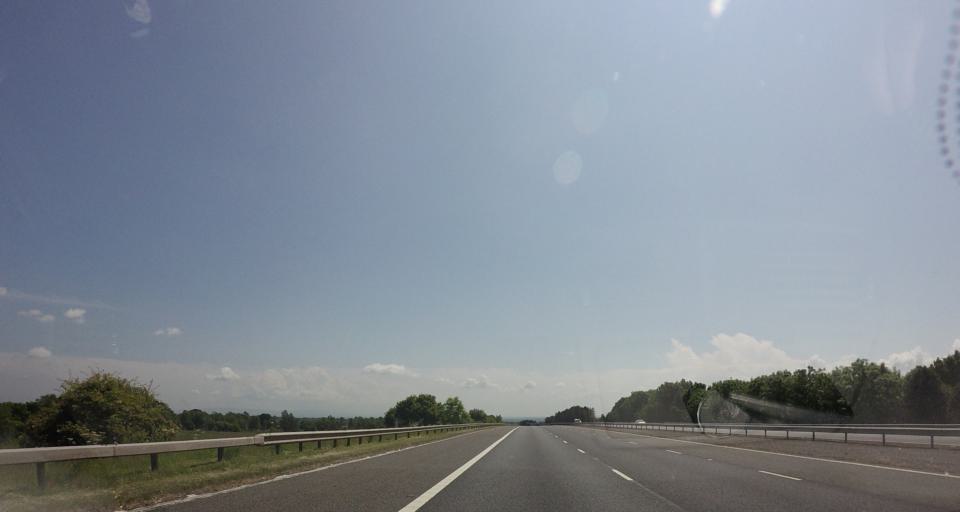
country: GB
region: Scotland
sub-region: Dumfries and Galloway
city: Gretna
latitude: 55.0226
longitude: -3.1247
